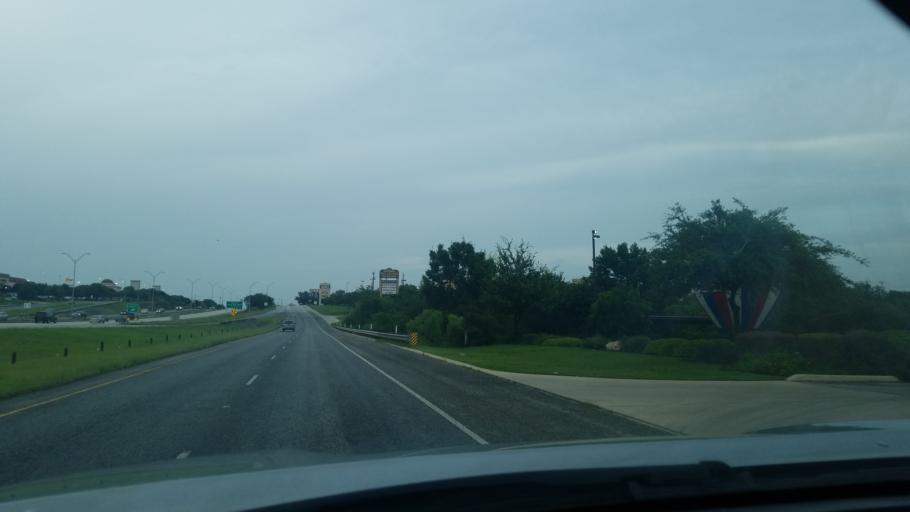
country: US
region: Texas
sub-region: Bexar County
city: Hollywood Park
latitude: 29.6081
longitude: -98.5175
